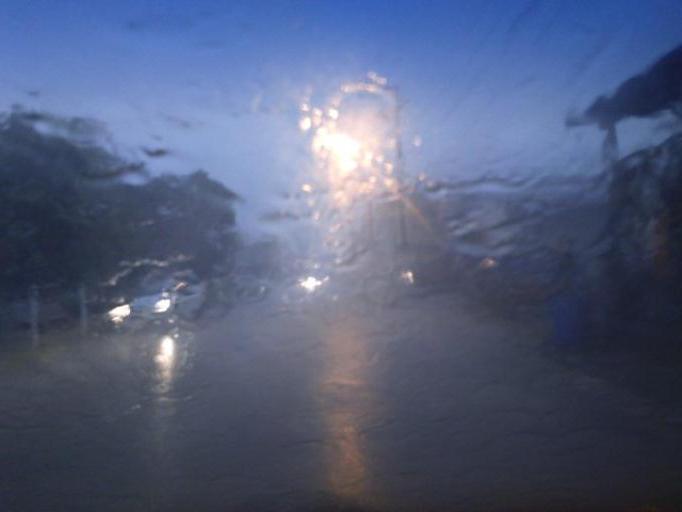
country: BR
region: Santa Catarina
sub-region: Itapema
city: Itapema
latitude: -27.1275
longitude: -48.6109
